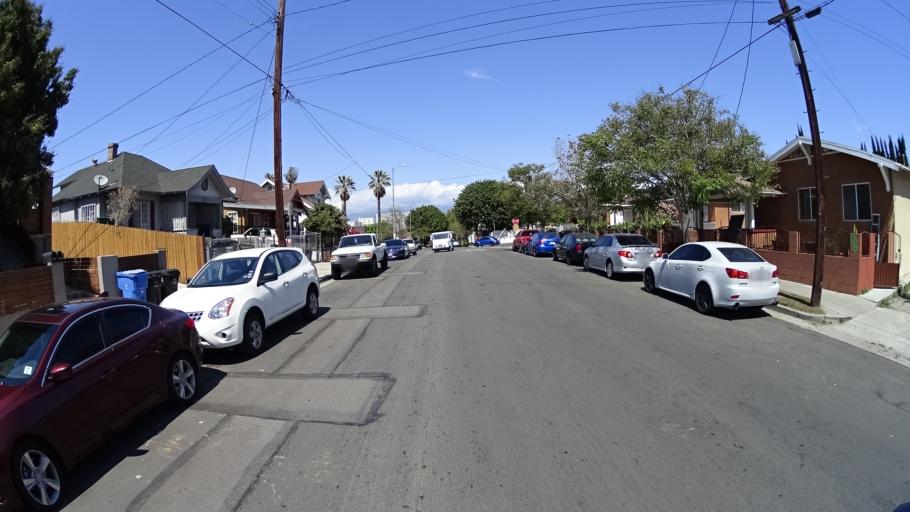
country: US
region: California
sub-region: Los Angeles County
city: Boyle Heights
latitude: 34.0511
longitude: -118.2099
